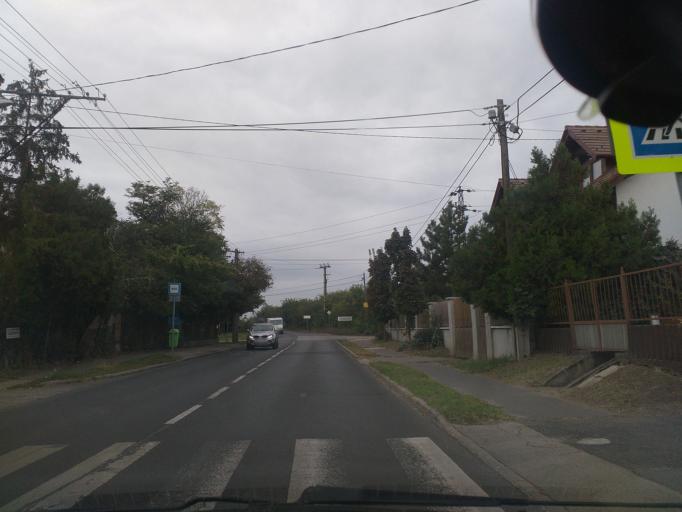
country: HU
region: Budapest
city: Budapest XVIII. keruelet
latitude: 47.4152
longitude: 19.1868
